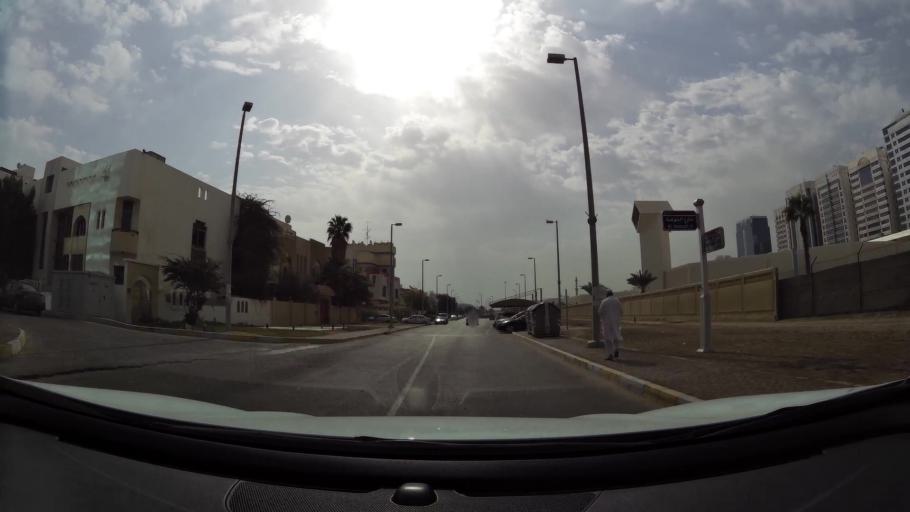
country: AE
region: Abu Dhabi
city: Abu Dhabi
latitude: 24.4620
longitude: 54.3817
